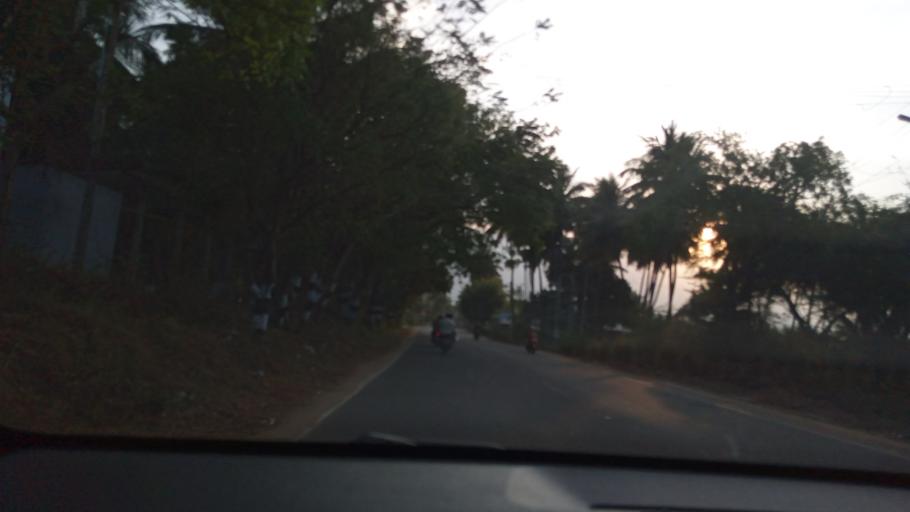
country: IN
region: Tamil Nadu
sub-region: Coimbatore
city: Perur
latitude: 10.9469
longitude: 76.7756
